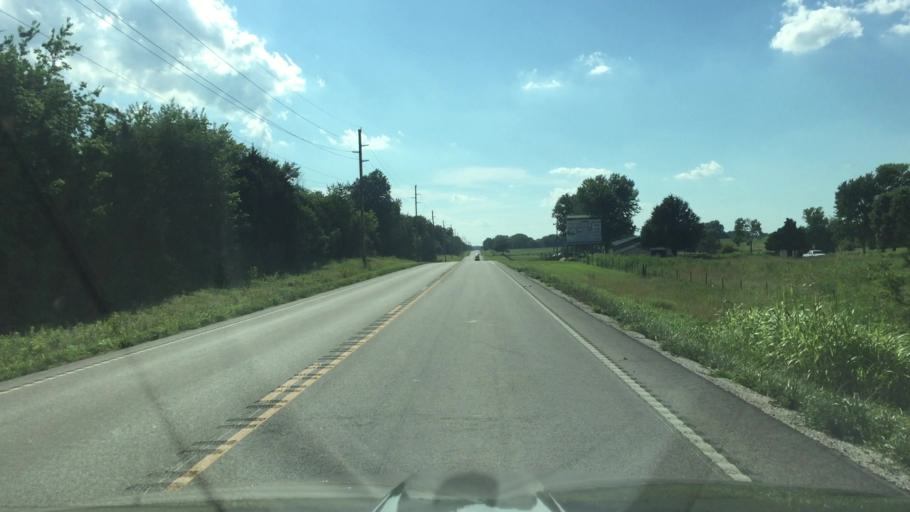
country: US
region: Missouri
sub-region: Morgan County
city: Versailles
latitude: 38.3951
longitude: -92.7194
